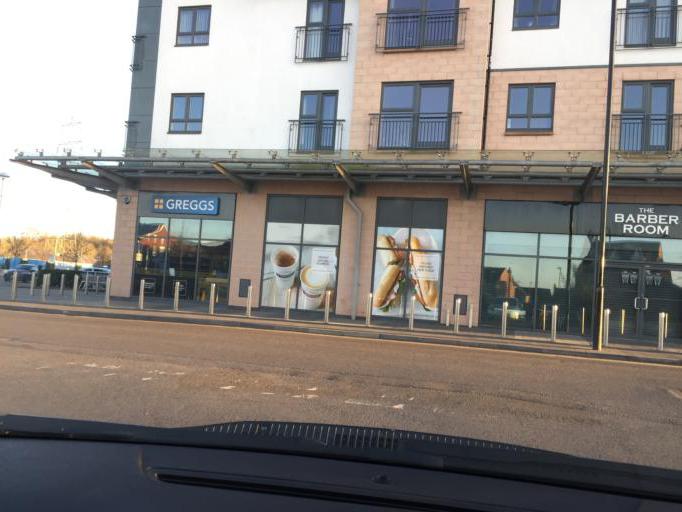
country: GB
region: England
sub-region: Warwickshire
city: Ryton on Dunsmore
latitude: 52.3985
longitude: -1.4337
